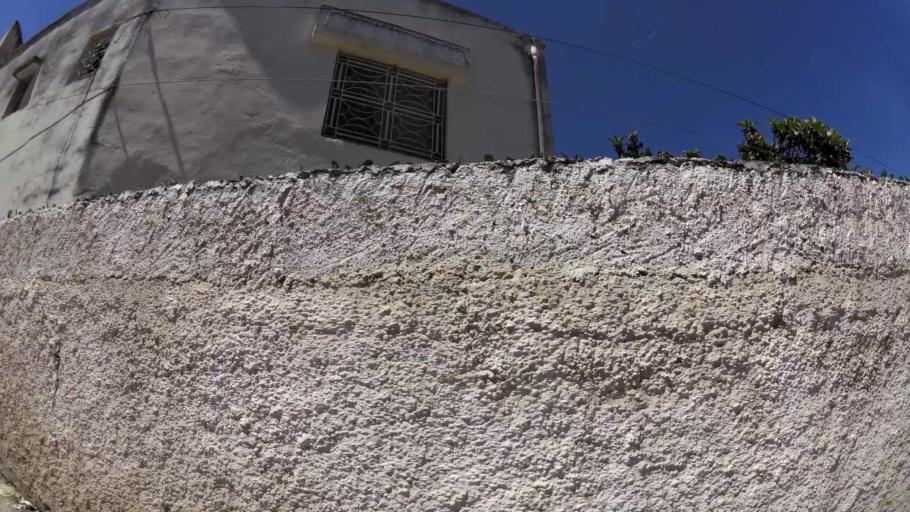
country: MA
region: Fes-Boulemane
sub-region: Fes
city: Fes
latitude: 34.0227
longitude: -4.9996
